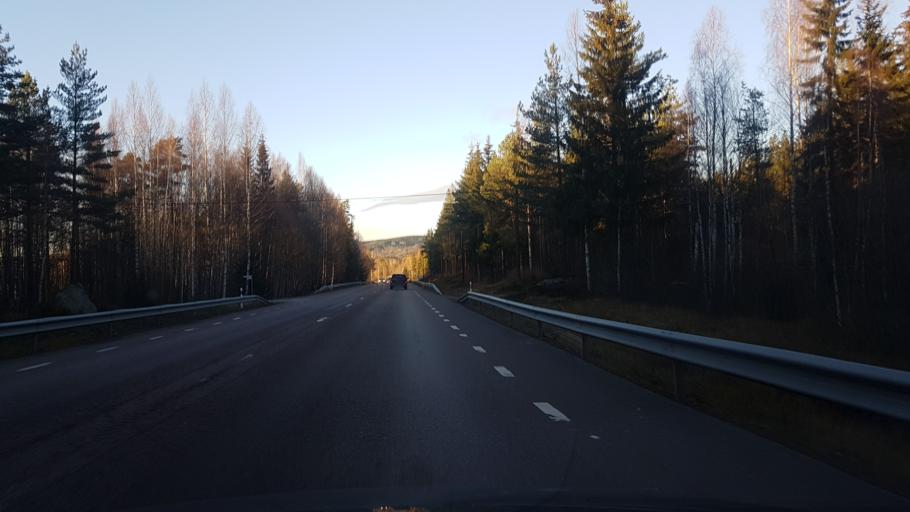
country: SE
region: Dalarna
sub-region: Faluns Kommun
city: Grycksbo
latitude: 60.7106
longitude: 15.4627
